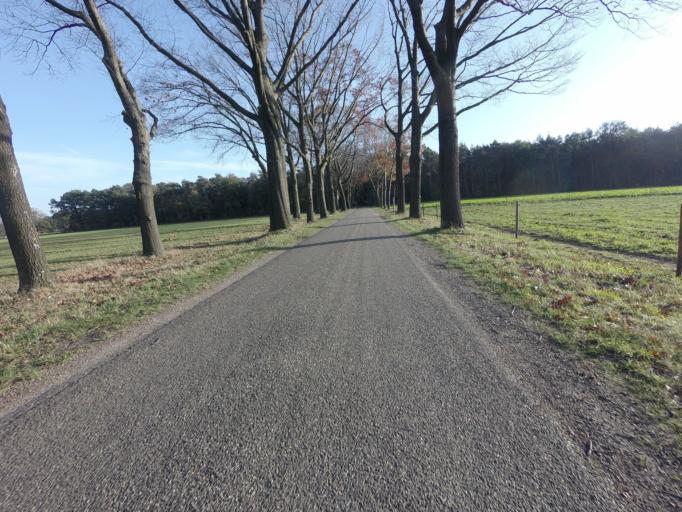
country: DE
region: North Rhine-Westphalia
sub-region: Regierungsbezirk Koln
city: Waldfeucht
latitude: 51.0937
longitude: 6.0058
